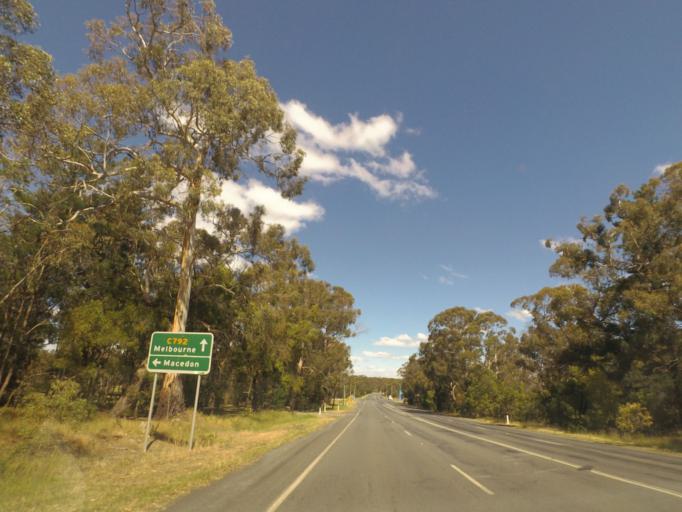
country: AU
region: Victoria
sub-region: Hume
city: Sunbury
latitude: -37.4306
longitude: 144.5569
